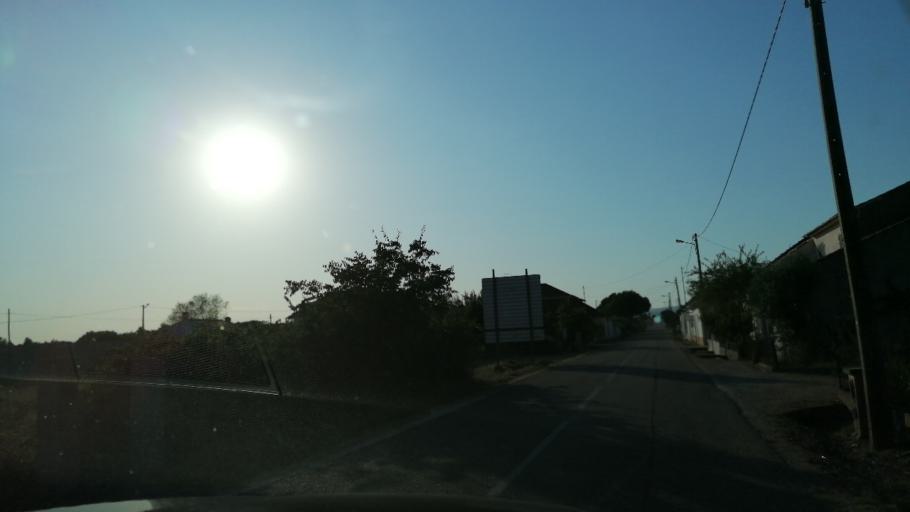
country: PT
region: Santarem
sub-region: Alcanena
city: Alcanena
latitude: 39.4517
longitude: -8.6236
